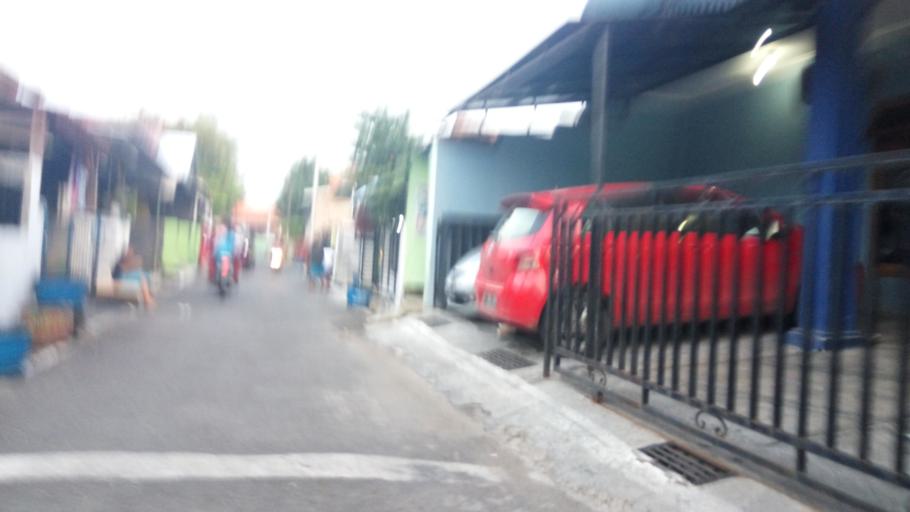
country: ID
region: Central Java
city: Semarang
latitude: -6.9840
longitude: 110.4032
